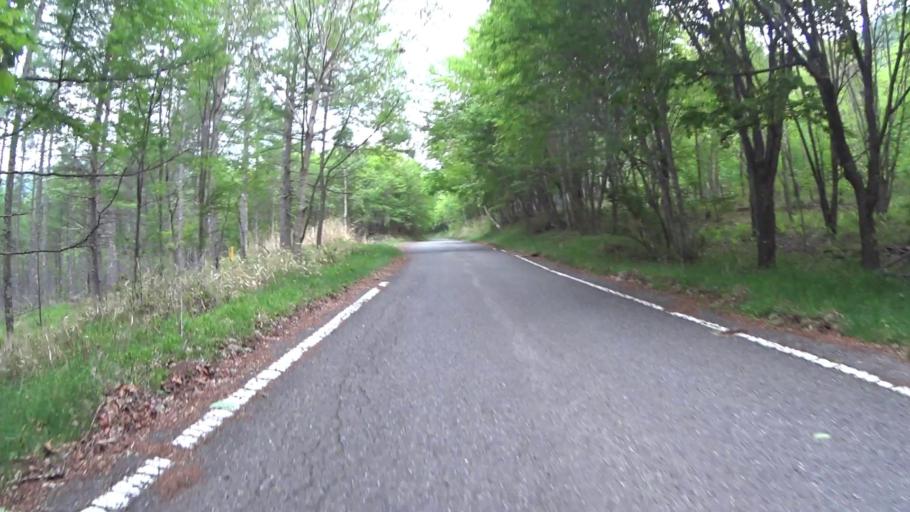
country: JP
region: Yamanashi
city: Kofu-shi
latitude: 35.8378
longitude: 138.5728
